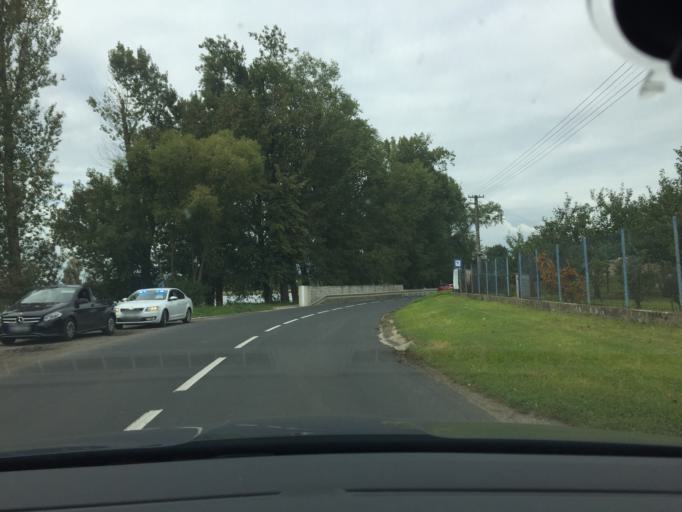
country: CZ
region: Ustecky
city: Kresice
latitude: 50.5097
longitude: 14.2266
